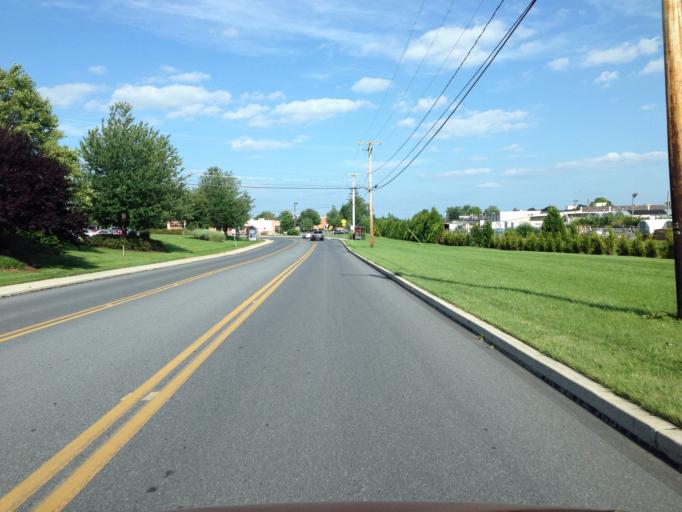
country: US
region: Pennsylvania
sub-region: Lancaster County
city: Lititz
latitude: 40.1293
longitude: -76.3095
